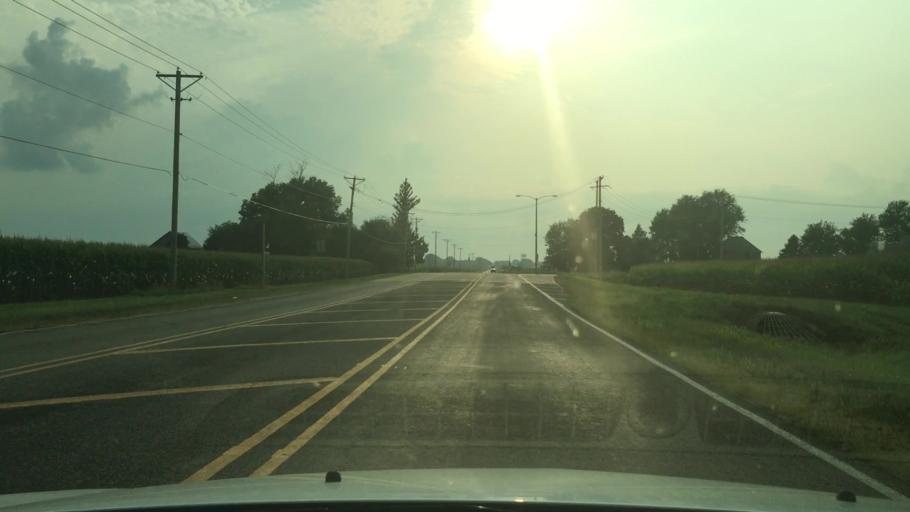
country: US
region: Illinois
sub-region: Ogle County
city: Rochelle
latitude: 41.9200
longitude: -89.0319
